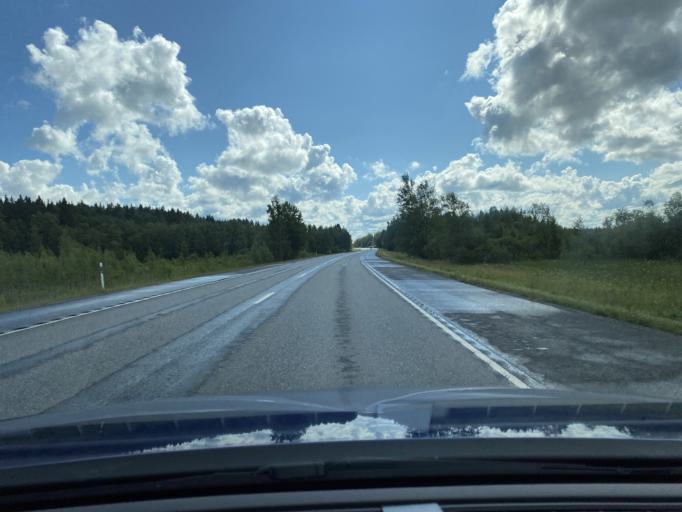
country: FI
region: Pirkanmaa
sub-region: Tampere
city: Lempaeaelae
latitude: 61.3385
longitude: 23.7854
